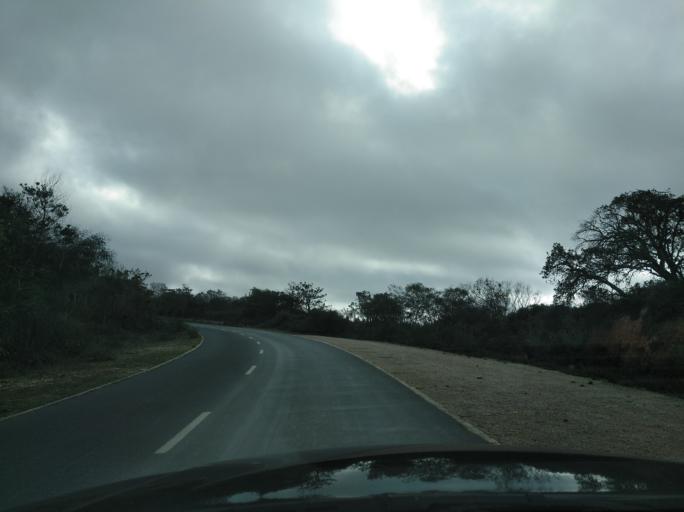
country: PT
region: Beja
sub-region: Odemira
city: Vila Nova de Milfontes
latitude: 37.7187
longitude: -8.7817
